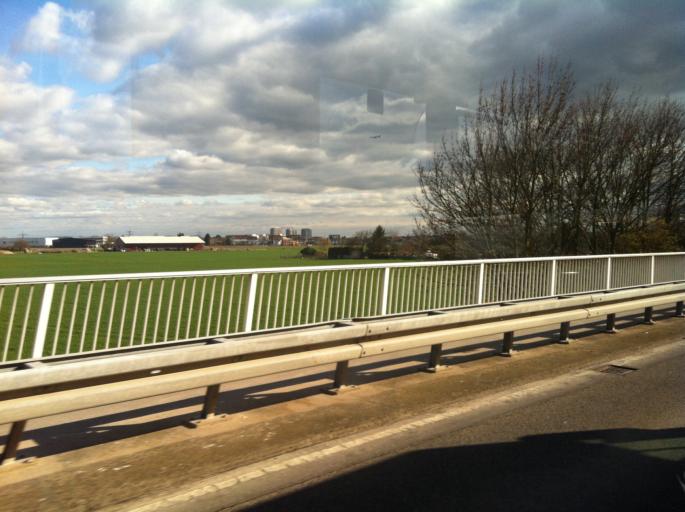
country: DE
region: Hesse
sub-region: Regierungsbezirk Darmstadt
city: Hochheim am Main
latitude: 50.0241
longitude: 8.3619
